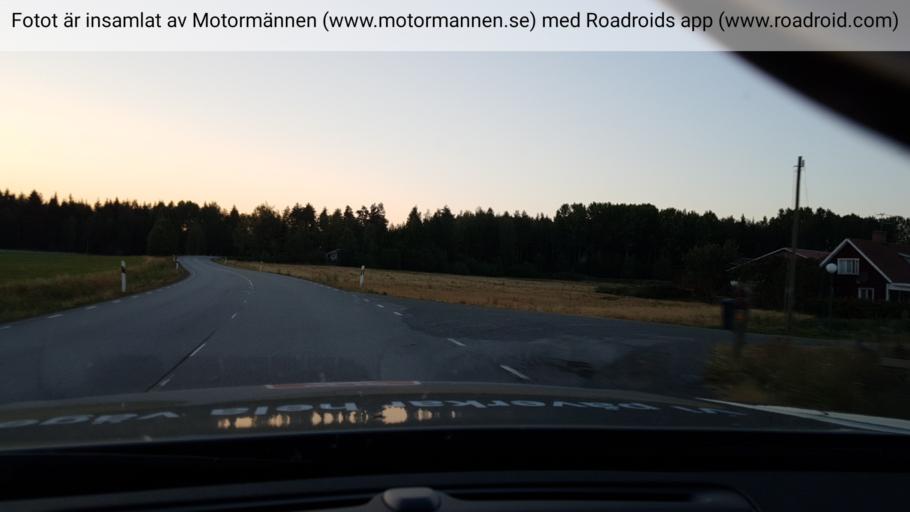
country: SE
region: Uppsala
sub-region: Heby Kommun
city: OEstervala
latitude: 60.1277
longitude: 17.2220
